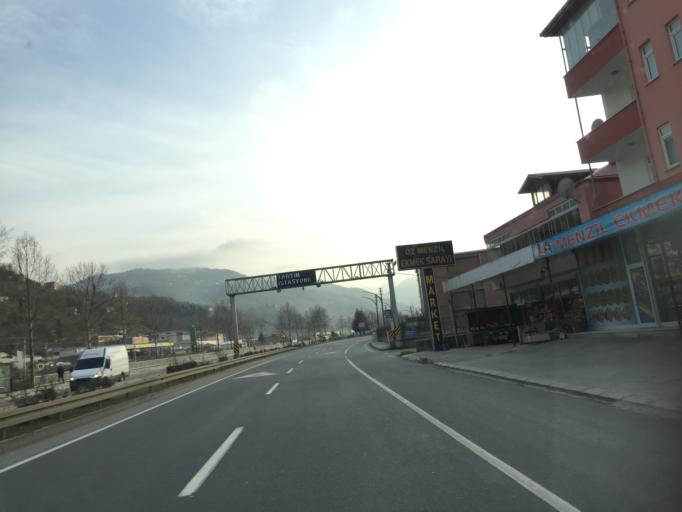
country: TR
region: Trabzon
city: Caglayan
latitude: 40.9204
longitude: 39.7247
